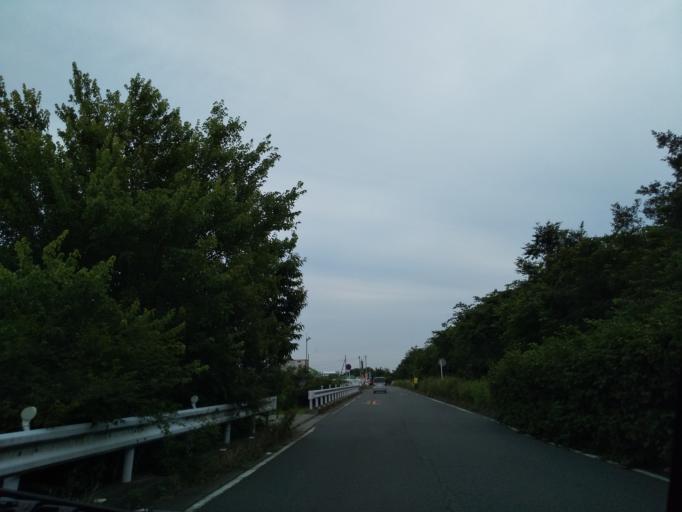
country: JP
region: Kanagawa
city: Zama
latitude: 35.4940
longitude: 139.3497
